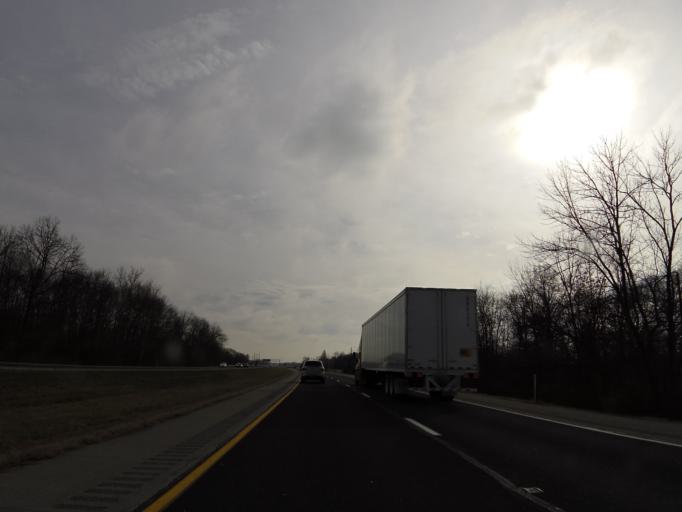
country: US
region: Indiana
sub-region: Marion County
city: Cumberland
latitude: 39.6904
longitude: -85.9850
